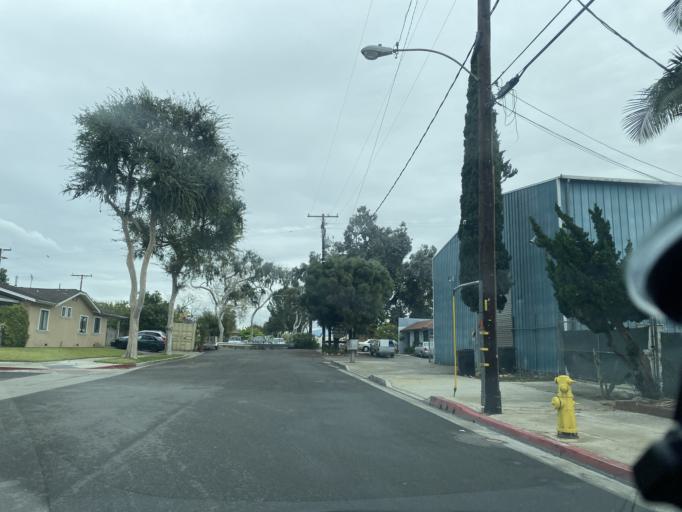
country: US
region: California
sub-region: Orange County
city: Fullerton
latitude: 33.8684
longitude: -117.9099
